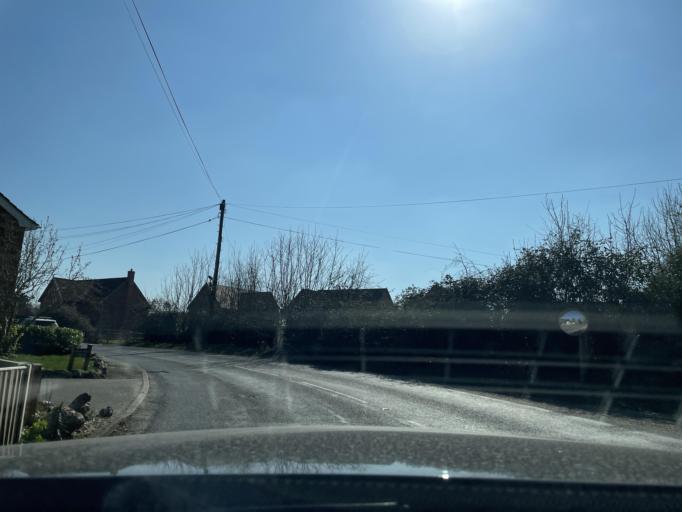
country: GB
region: England
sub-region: Norfolk
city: Hingham
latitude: 52.6119
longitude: 1.0173
